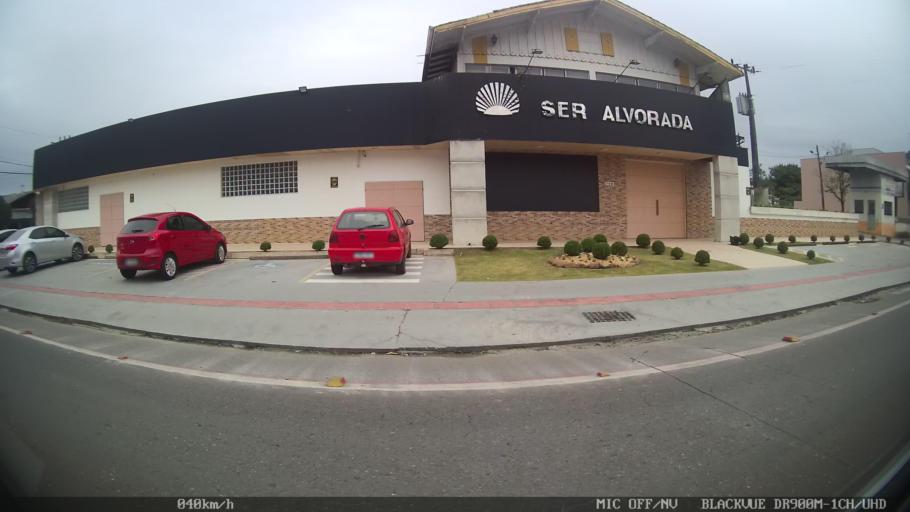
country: BR
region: Santa Catarina
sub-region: Joinville
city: Joinville
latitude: -26.2760
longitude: -48.8342
